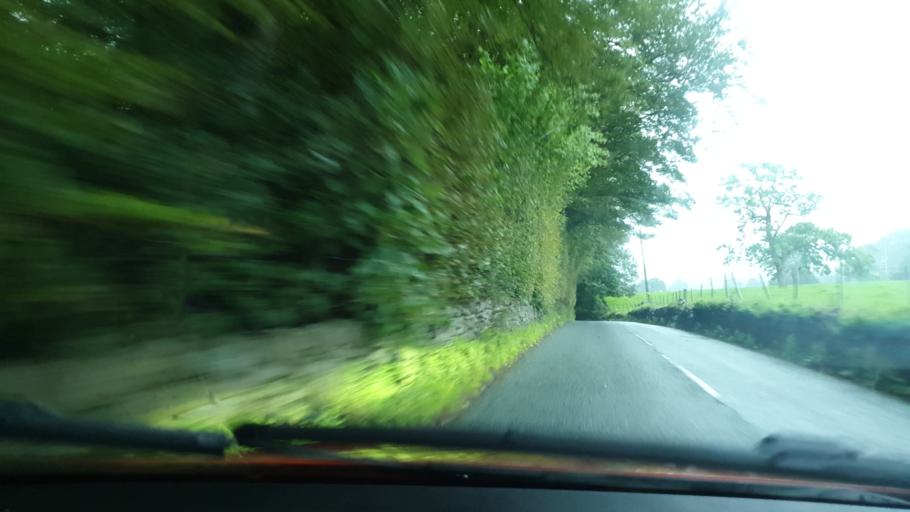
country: GB
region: England
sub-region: Cumbria
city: Ulverston
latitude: 54.2523
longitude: -3.0711
